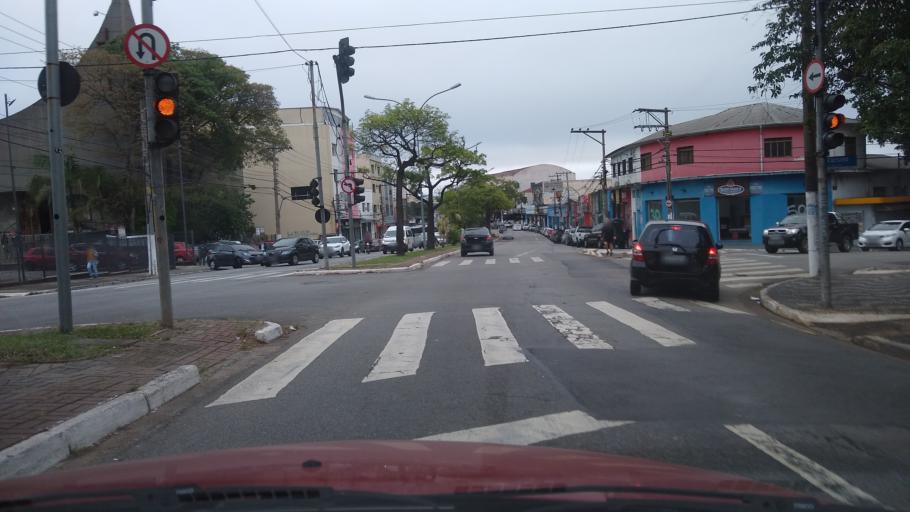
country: BR
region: Sao Paulo
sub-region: Diadema
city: Diadema
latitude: -23.6184
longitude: -46.6188
